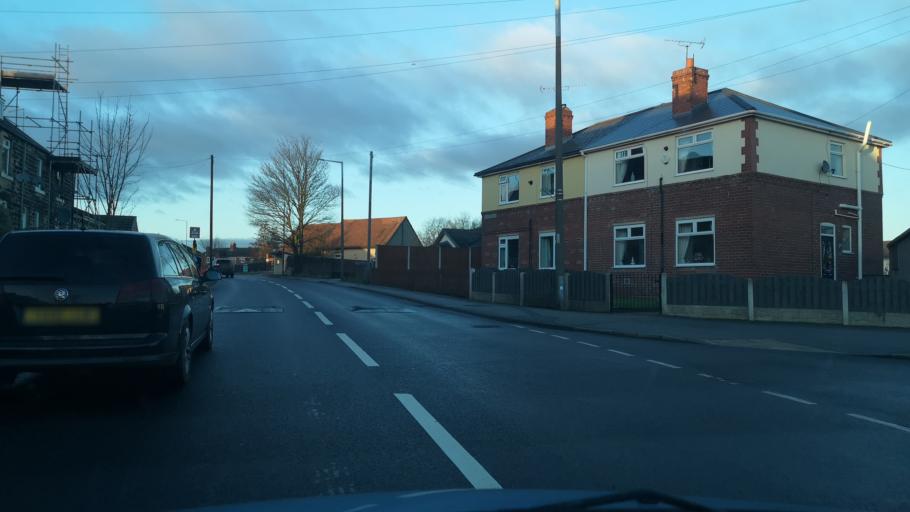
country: GB
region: England
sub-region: Barnsley
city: Great Houghton
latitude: 53.5511
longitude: -1.3468
